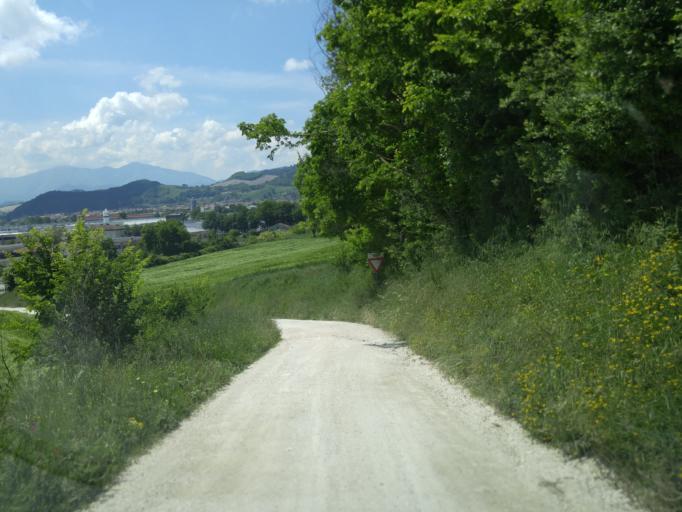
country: IT
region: The Marches
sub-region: Provincia di Pesaro e Urbino
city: Fermignano
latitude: 43.7003
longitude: 12.6608
